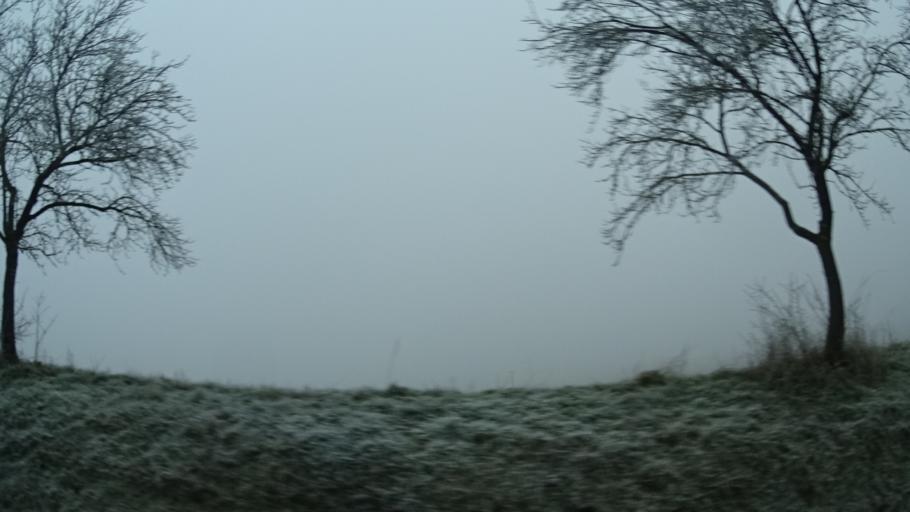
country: DE
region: Bavaria
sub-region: Regierungsbezirk Unterfranken
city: Donnersdorf
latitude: 49.9516
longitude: 10.4283
